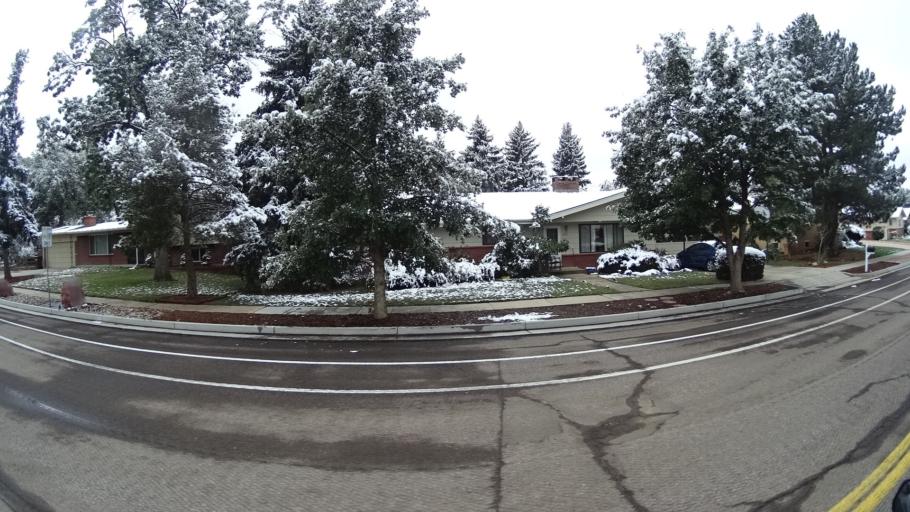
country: US
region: Colorado
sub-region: El Paso County
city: Colorado Springs
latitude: 38.8903
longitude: -104.7822
